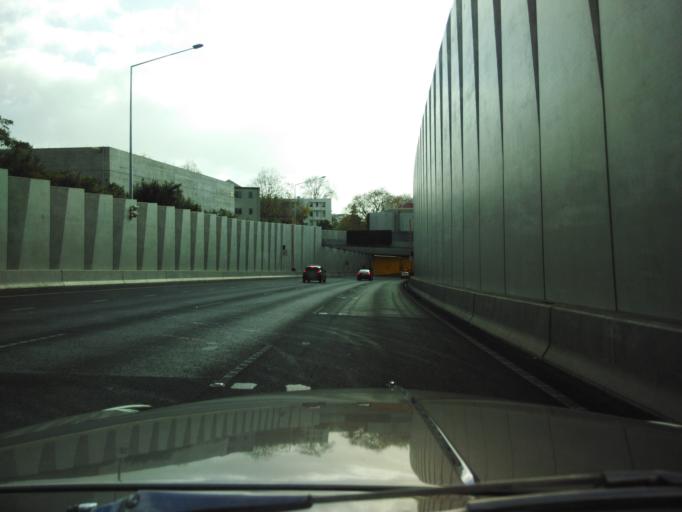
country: NZ
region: Auckland
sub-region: Auckland
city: Auckland
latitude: -36.8500
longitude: 174.7533
